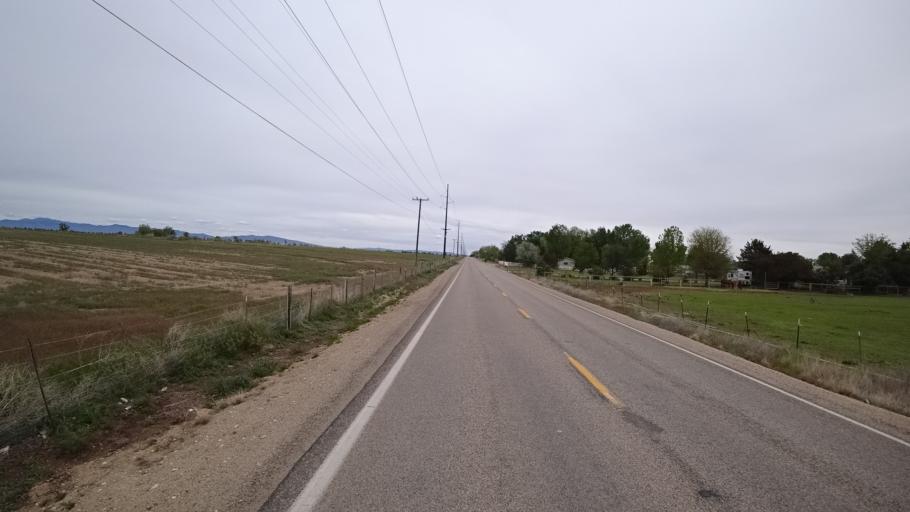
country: US
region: Idaho
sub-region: Ada County
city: Kuna
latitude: 43.4883
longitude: -116.3316
